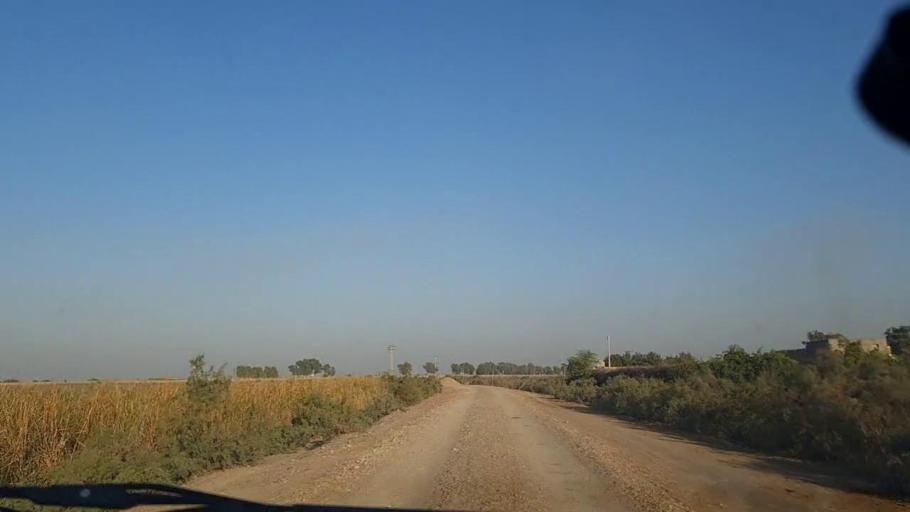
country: PK
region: Sindh
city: Berani
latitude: 25.6998
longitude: 68.9273
